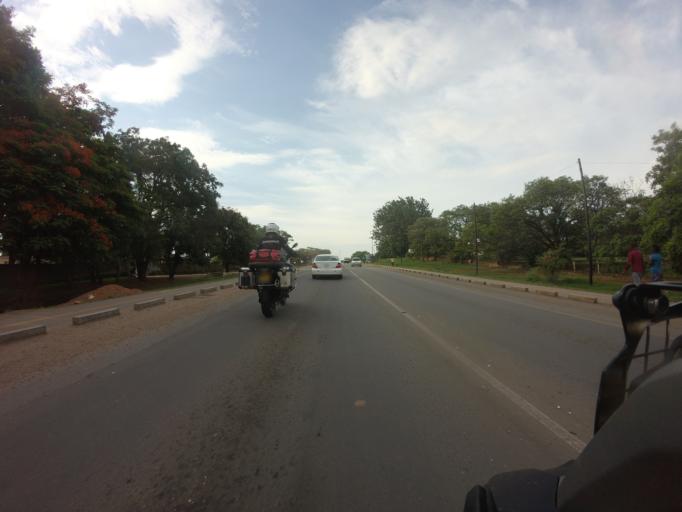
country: ZM
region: Lusaka
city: Lusaka
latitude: -15.5527
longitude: 28.2703
